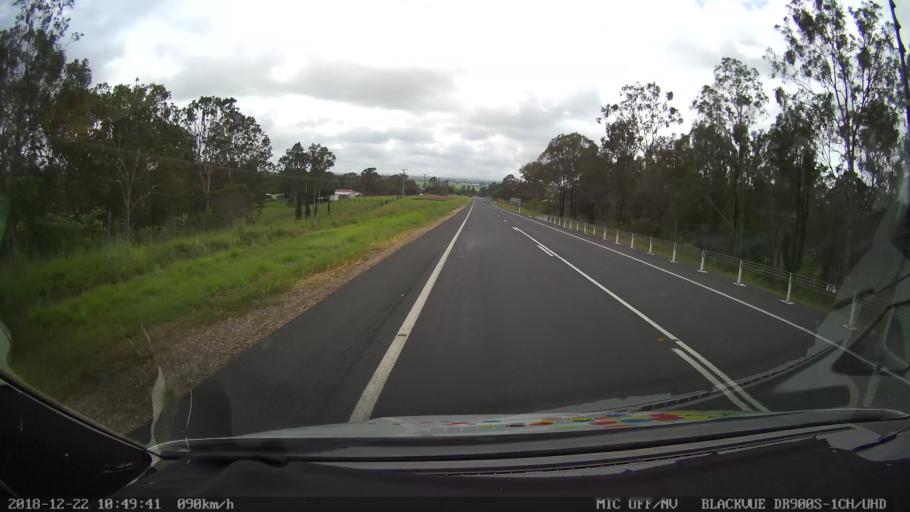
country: AU
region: New South Wales
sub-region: Clarence Valley
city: South Grafton
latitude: -29.6838
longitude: 152.8713
